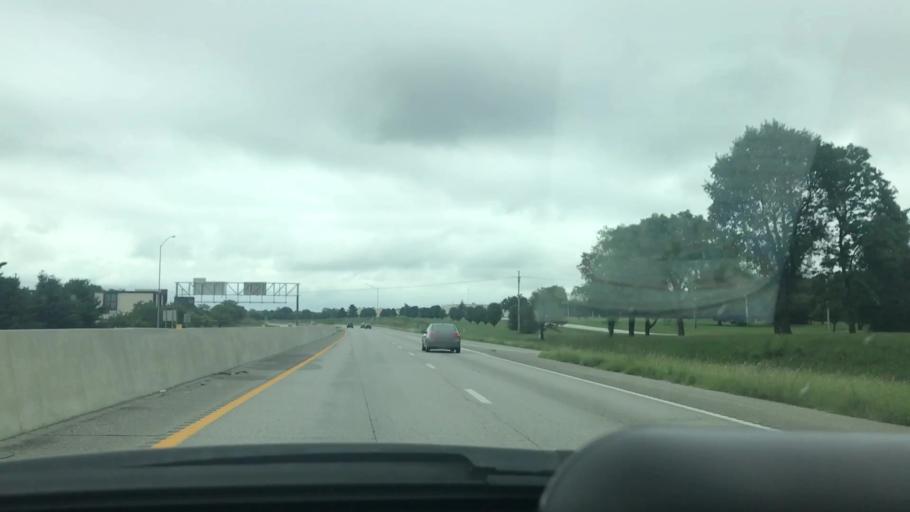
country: US
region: Missouri
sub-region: Jasper County
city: Duquesne
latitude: 37.0465
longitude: -94.4756
